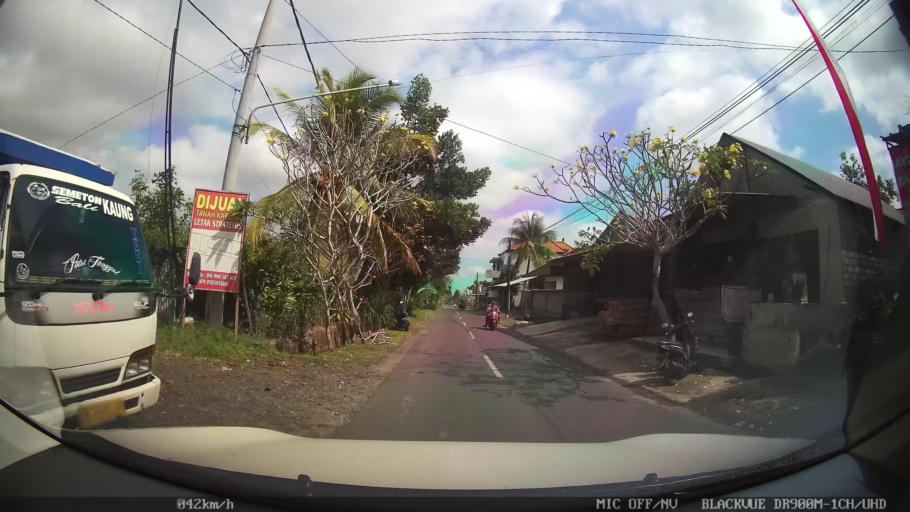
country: ID
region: Bali
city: Banjar Pesalakan
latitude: -8.5097
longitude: 115.3129
